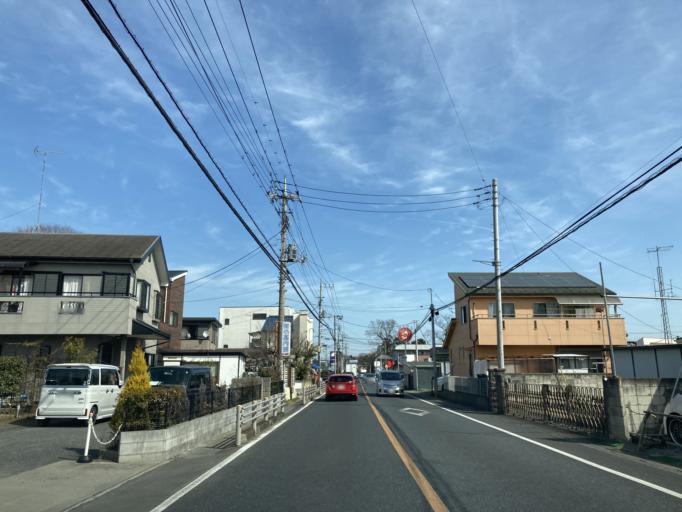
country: JP
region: Saitama
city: Tokorozawa
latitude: 35.8131
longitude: 139.4810
